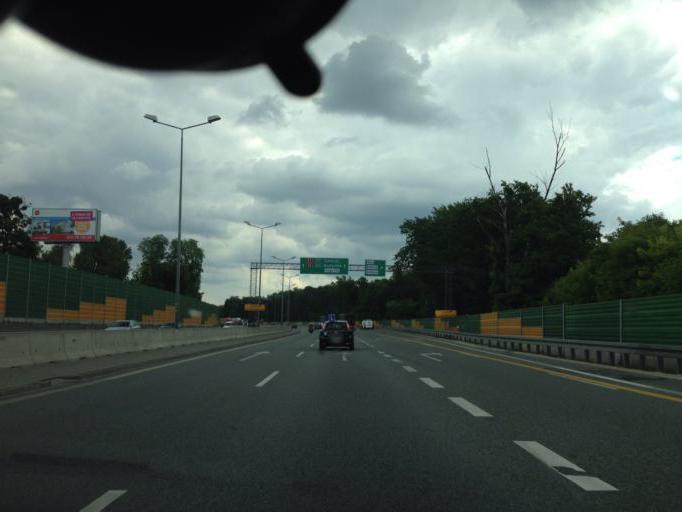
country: PL
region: Masovian Voivodeship
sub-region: Warszawa
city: Bemowo
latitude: 52.2504
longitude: 20.9398
